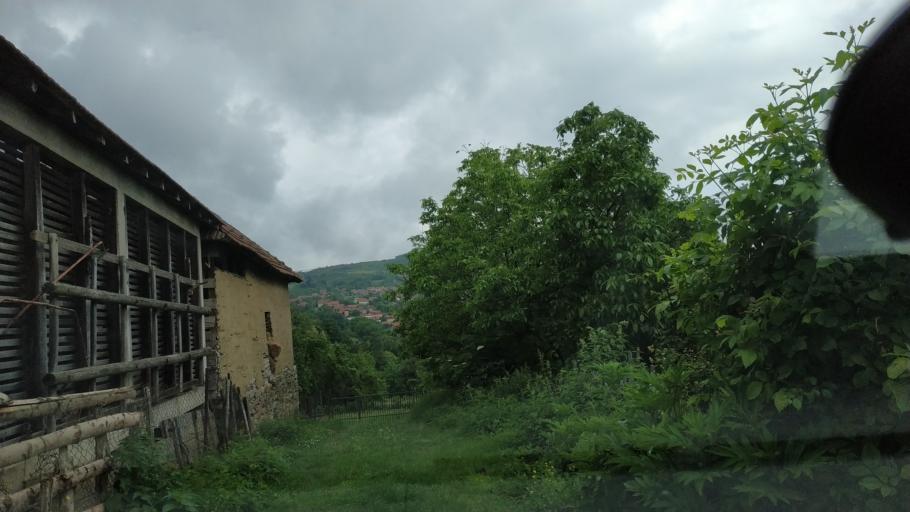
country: RS
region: Central Serbia
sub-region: Toplicki Okrug
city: Prokuplje
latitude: 43.3953
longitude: 21.5533
